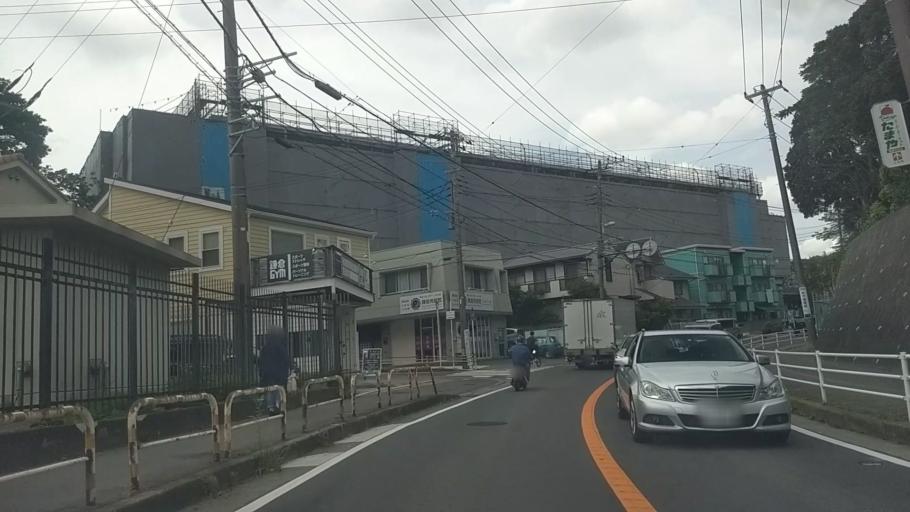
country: JP
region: Kanagawa
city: Fujisawa
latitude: 35.3239
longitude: 139.5063
